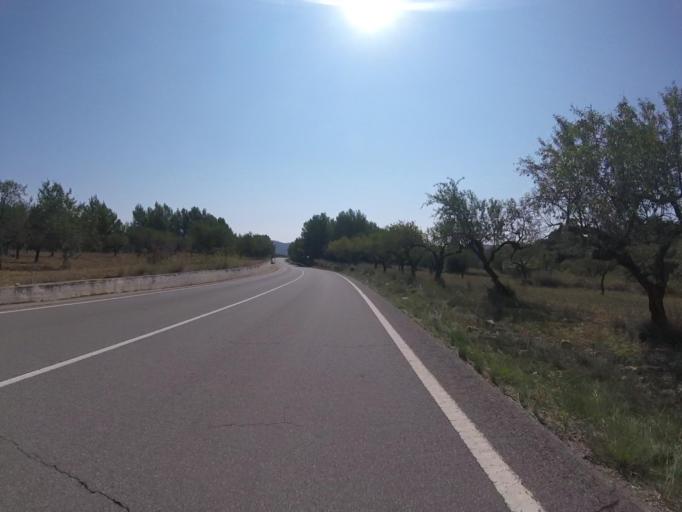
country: ES
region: Valencia
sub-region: Provincia de Castello
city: Adzaneta
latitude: 40.2349
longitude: -0.1801
